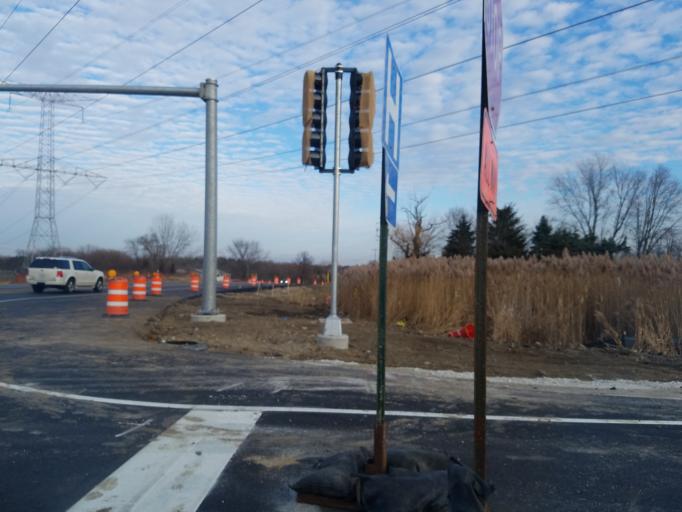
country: US
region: Illinois
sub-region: Will County
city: New Lenox
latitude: 41.5486
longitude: -87.9427
